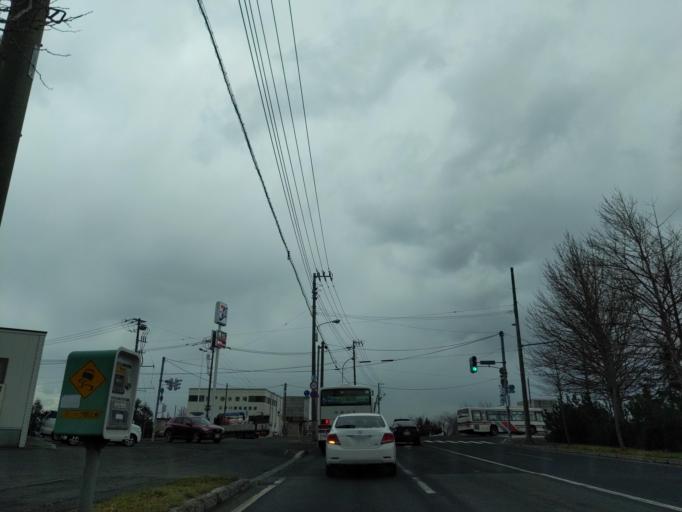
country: JP
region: Hokkaido
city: Ishikari
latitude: 43.1582
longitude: 141.3604
